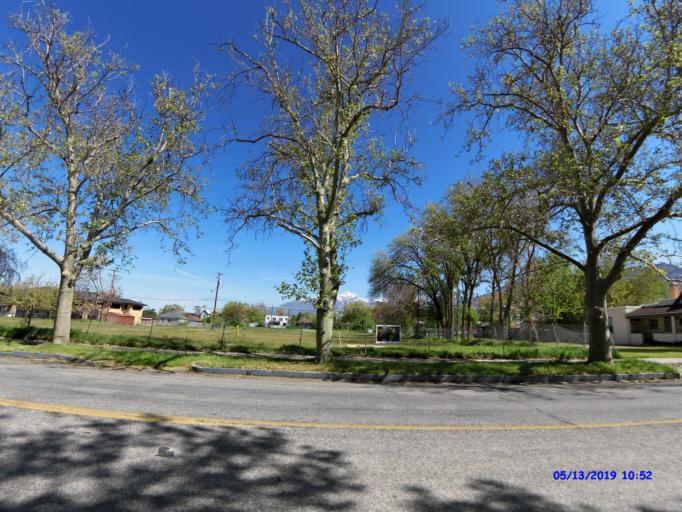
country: US
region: Utah
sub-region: Weber County
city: Ogden
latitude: 41.2227
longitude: -111.9661
